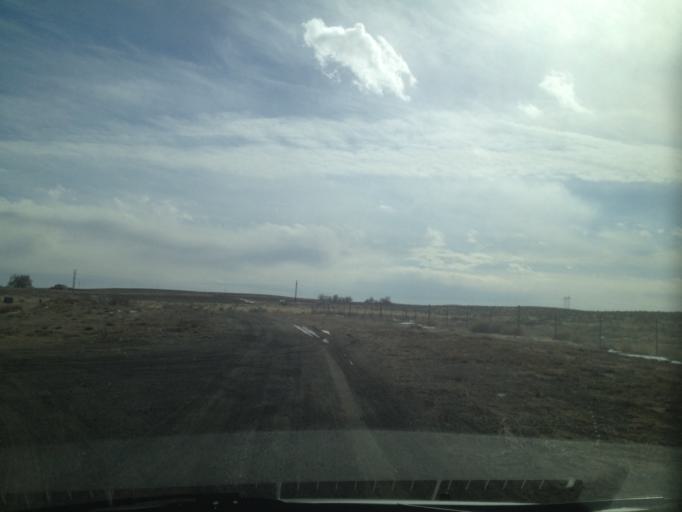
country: US
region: Colorado
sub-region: Weld County
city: Keenesburg
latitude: 40.2883
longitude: -104.2625
